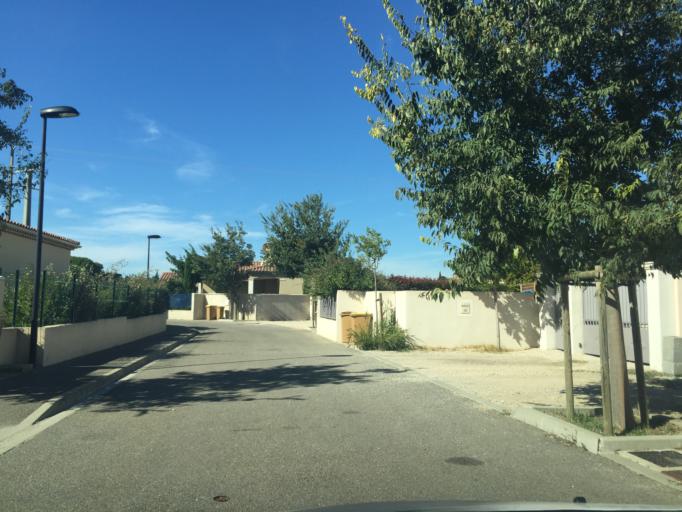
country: FR
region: Provence-Alpes-Cote d'Azur
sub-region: Departement du Vaucluse
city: Orange
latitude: 44.1454
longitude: 4.7911
